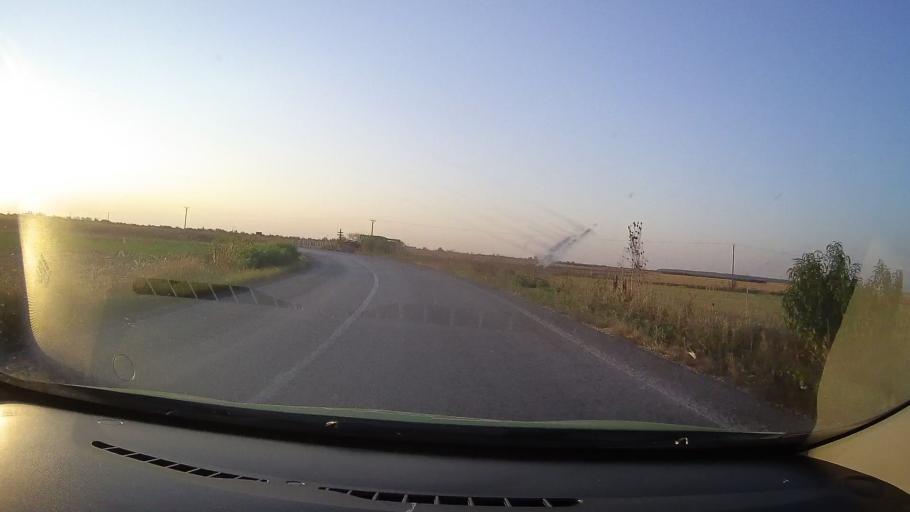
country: RO
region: Arad
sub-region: Comuna Ineu
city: Ineu
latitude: 46.4343
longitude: 21.8580
